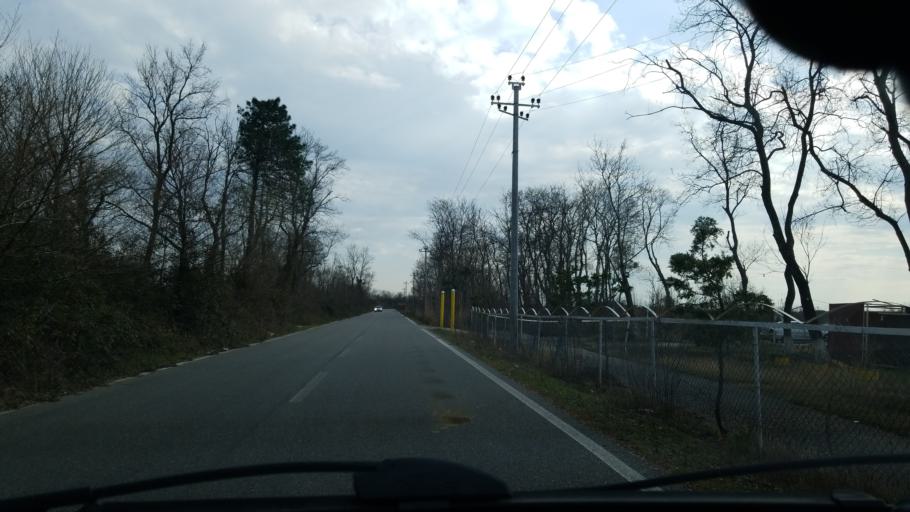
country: AL
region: Lezhe
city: Shengjin
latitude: 41.7779
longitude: 19.6033
